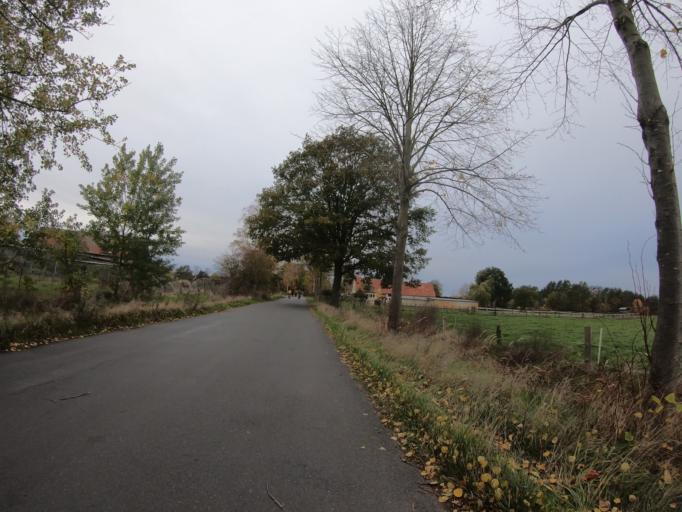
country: DE
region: Lower Saxony
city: Isenbuttel
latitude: 52.4684
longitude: 10.5860
